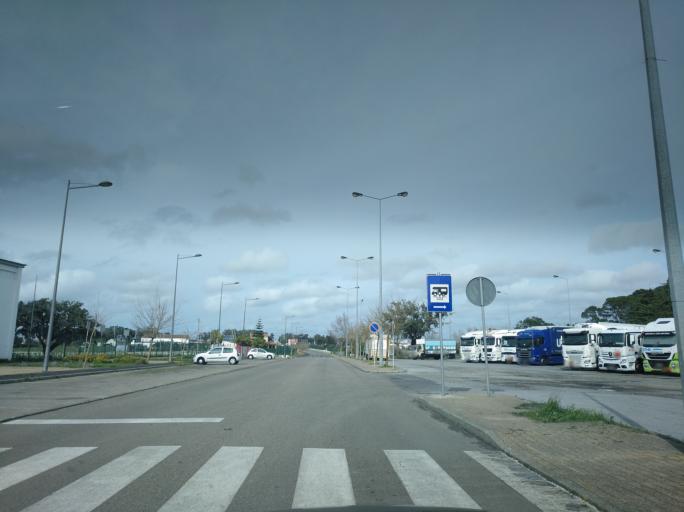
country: PT
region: Setubal
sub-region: Grandola
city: Grandola
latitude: 38.1844
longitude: -8.5643
